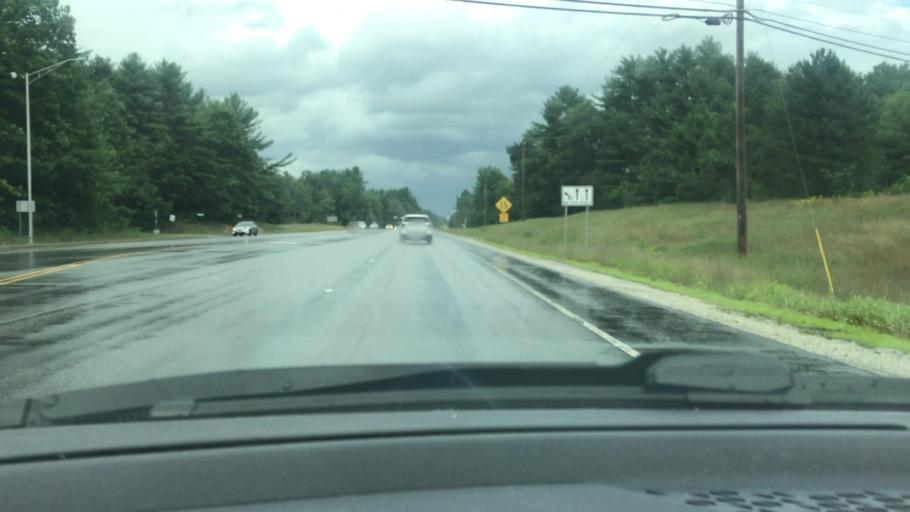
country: US
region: New Hampshire
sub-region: Merrimack County
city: East Concord
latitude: 43.2362
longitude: -71.4695
